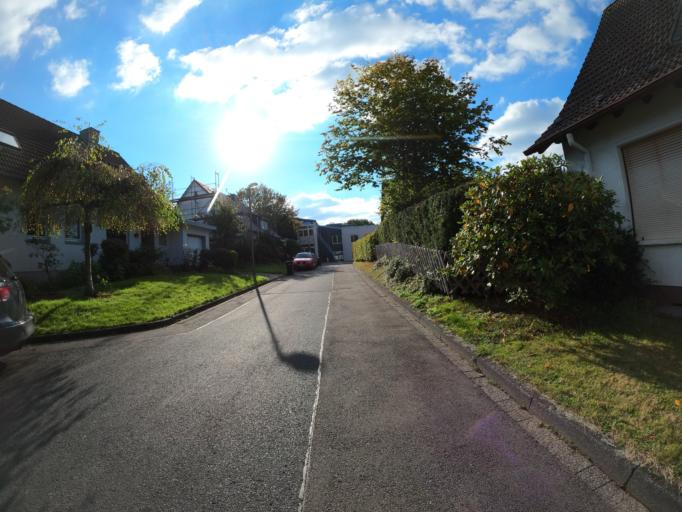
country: DE
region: North Rhine-Westphalia
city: Radevormwald
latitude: 51.2066
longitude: 7.3479
